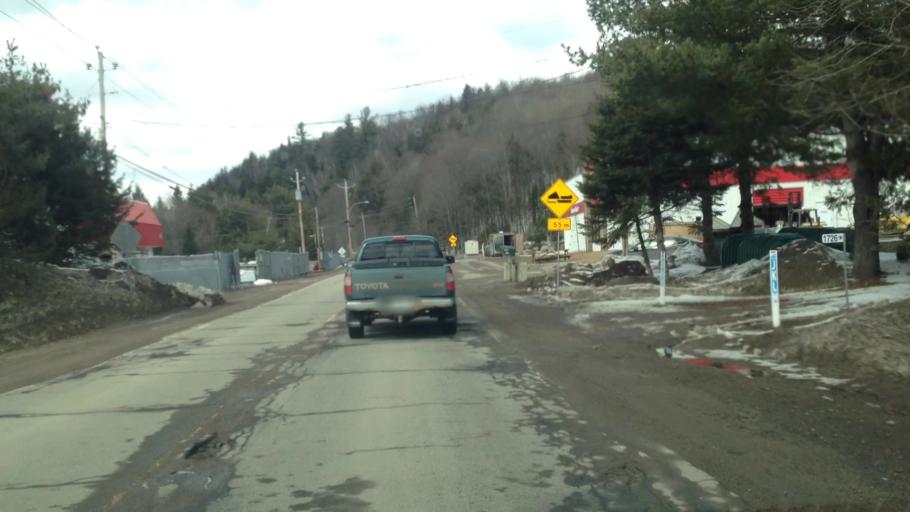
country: CA
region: Quebec
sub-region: Laurentides
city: Brownsburg-Chatham
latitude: 45.7298
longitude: -74.4849
